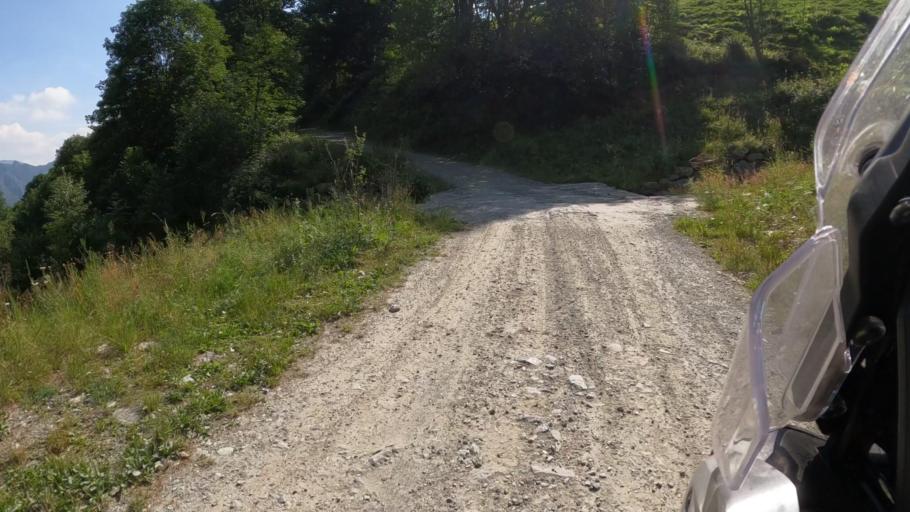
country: IT
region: Piedmont
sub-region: Provincia di Torino
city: Lemie
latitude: 45.2016
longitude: 7.3048
